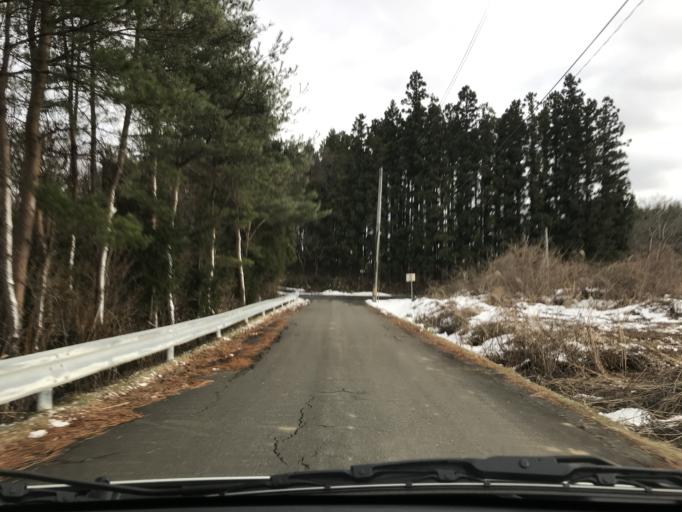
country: JP
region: Iwate
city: Ichinoseki
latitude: 38.9860
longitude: 141.0053
